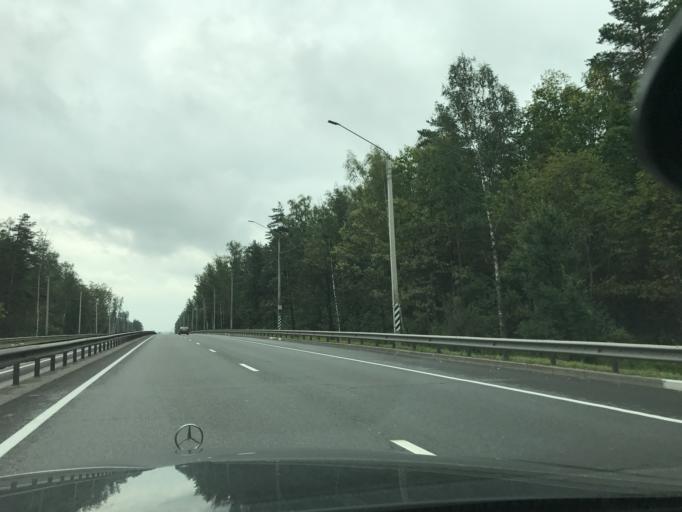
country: RU
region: Vladimir
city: Vyazniki
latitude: 56.2205
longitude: 42.1607
